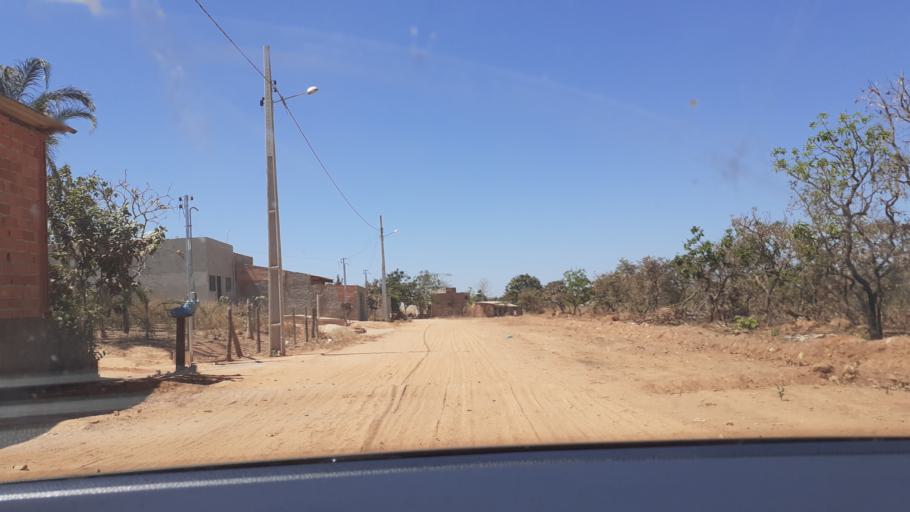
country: BR
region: Goias
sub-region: Caldas Novas
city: Caldas Novas
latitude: -17.7449
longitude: -48.6522
